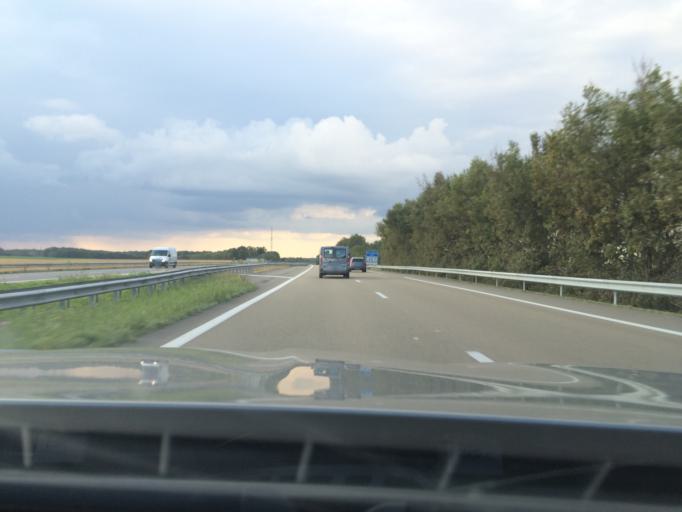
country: FR
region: Ile-de-France
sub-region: Departement de Seine-et-Marne
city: Egreville
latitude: 48.1557
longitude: 2.8926
